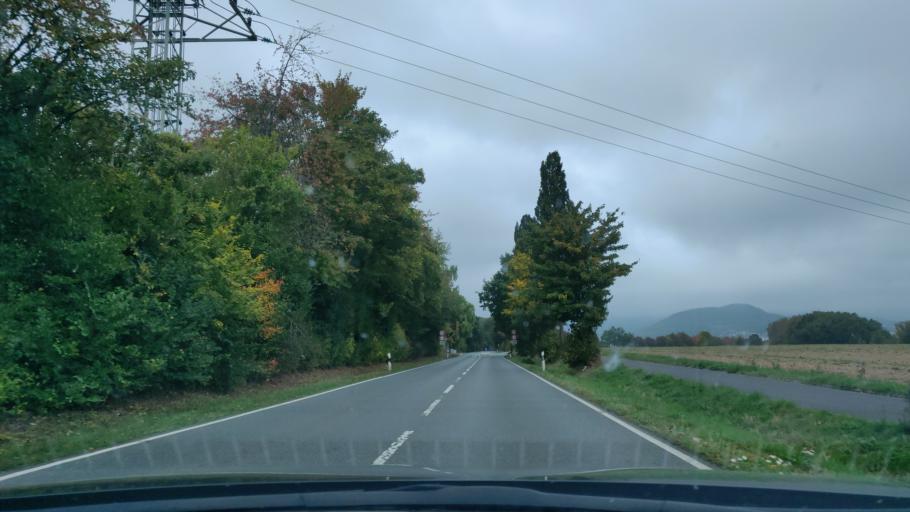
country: DE
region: Hesse
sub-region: Regierungsbezirk Kassel
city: Baunatal
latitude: 51.2332
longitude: 9.4235
